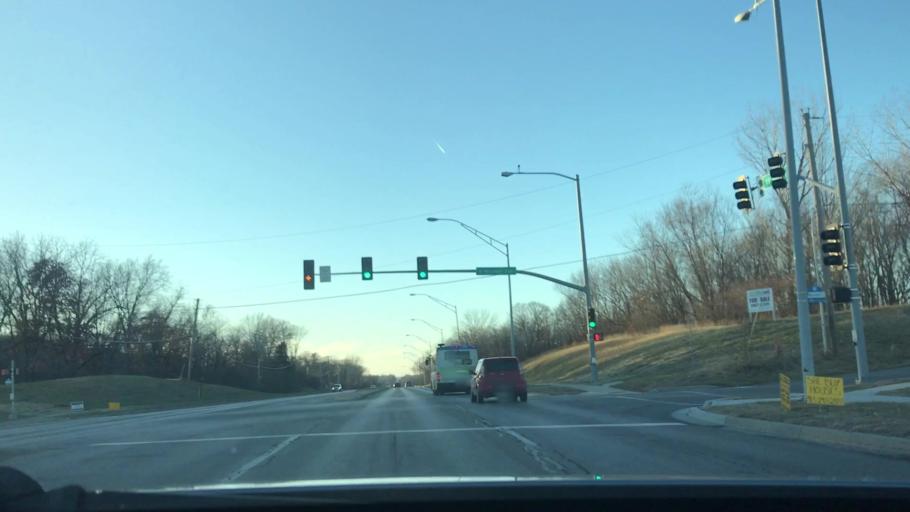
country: US
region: Missouri
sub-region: Clay County
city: Gladstone
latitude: 39.2464
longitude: -94.6072
